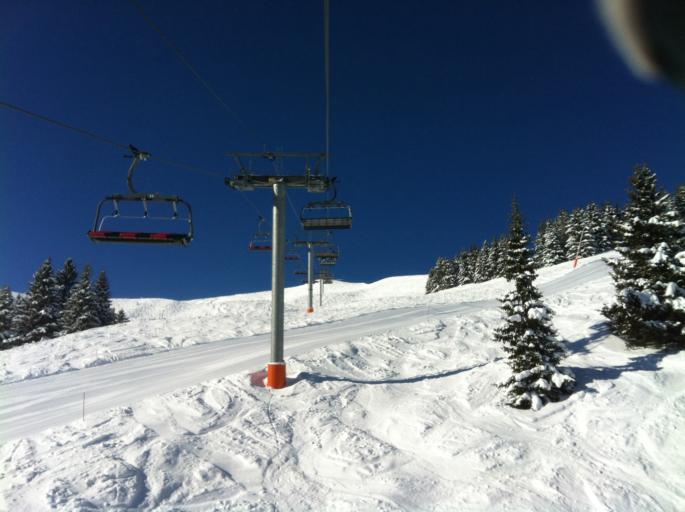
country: FR
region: Rhone-Alpes
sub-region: Departement de la Haute-Savoie
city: Les Contamines-Montjoie
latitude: 45.8474
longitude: 6.6911
